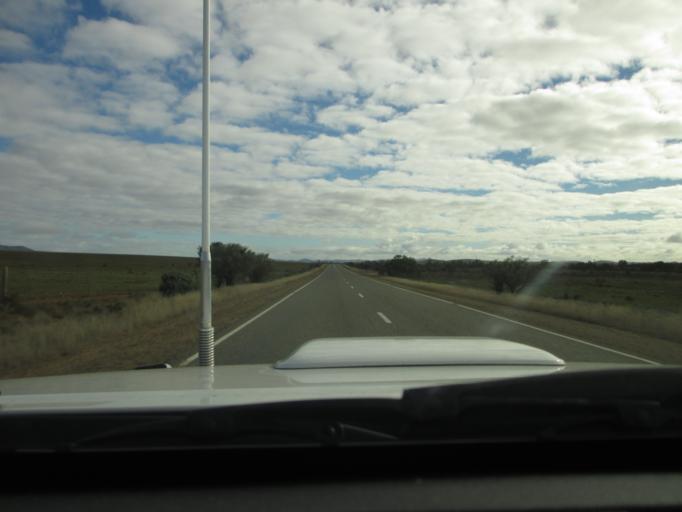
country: AU
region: South Australia
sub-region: Flinders Ranges
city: Quorn
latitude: -32.4059
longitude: 138.5175
